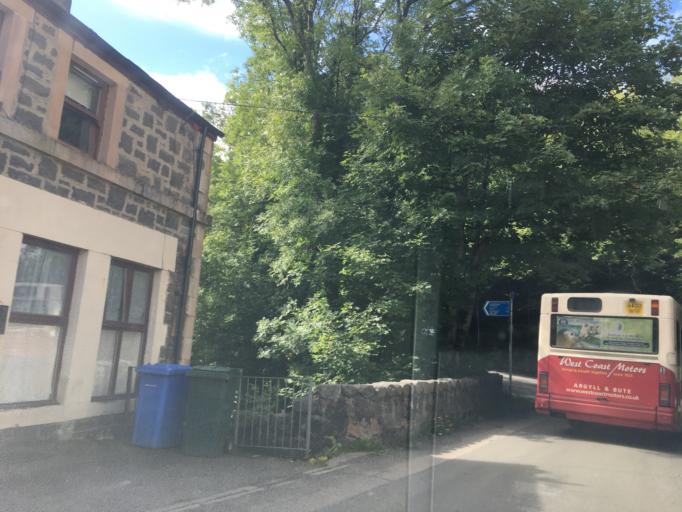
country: GB
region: Scotland
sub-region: Argyll and Bute
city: Oban
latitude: 56.4528
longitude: -5.3856
